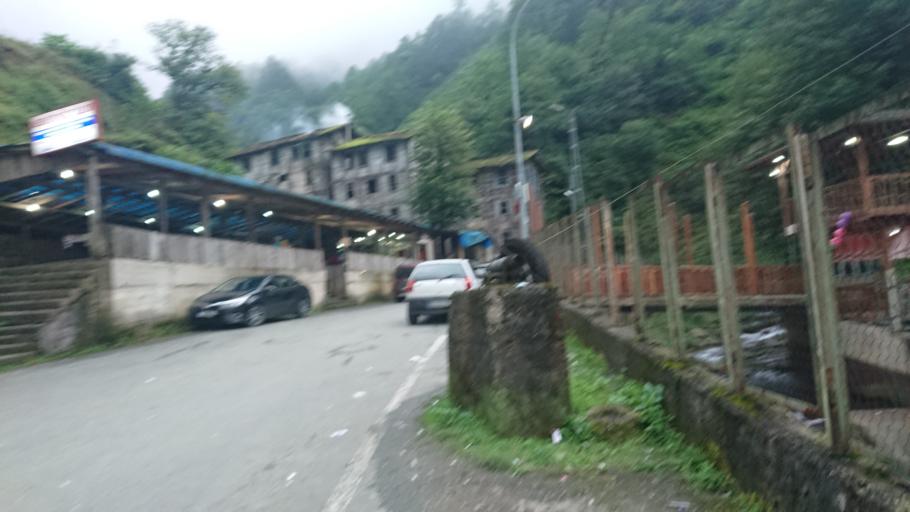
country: TR
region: Rize
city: Ikizdere
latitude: 40.8597
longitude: 40.5866
